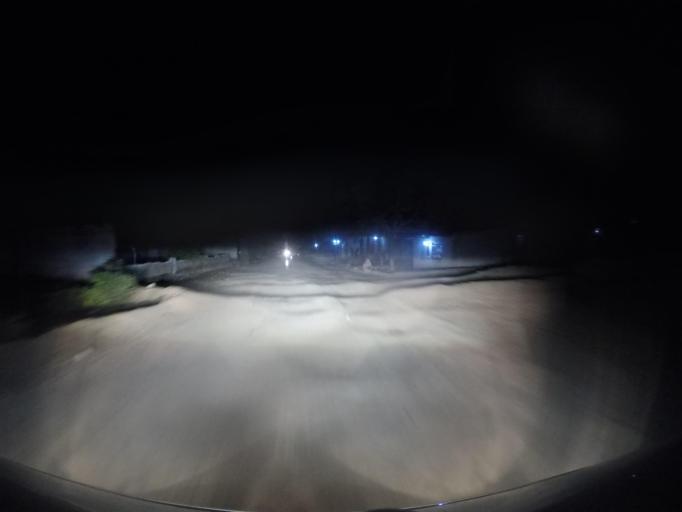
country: TL
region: Viqueque
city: Viqueque
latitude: -8.8011
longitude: 126.5517
